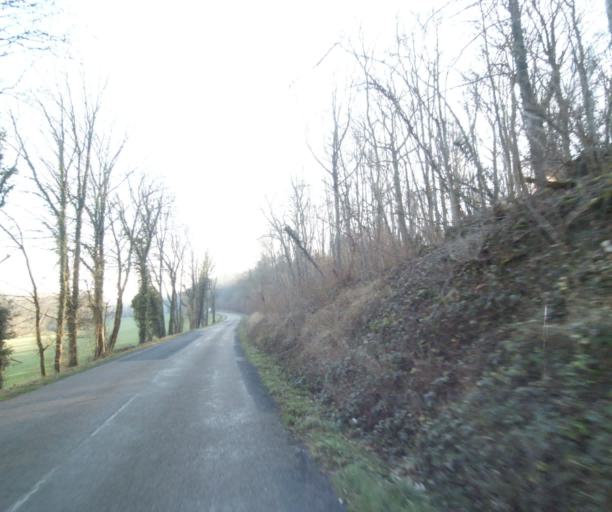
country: FR
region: Champagne-Ardenne
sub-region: Departement de la Haute-Marne
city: Bienville
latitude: 48.5675
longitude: 5.0795
